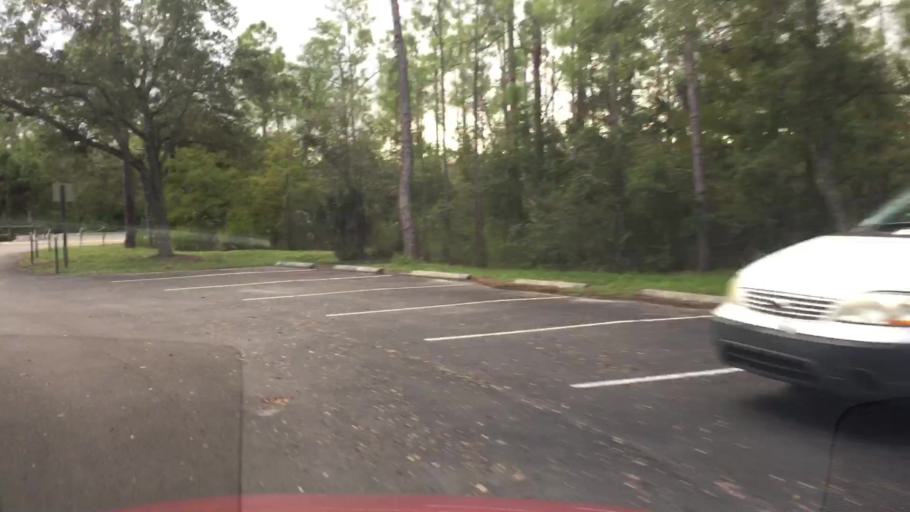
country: US
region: Florida
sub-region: Lee County
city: Villas
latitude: 26.5711
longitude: -81.8267
